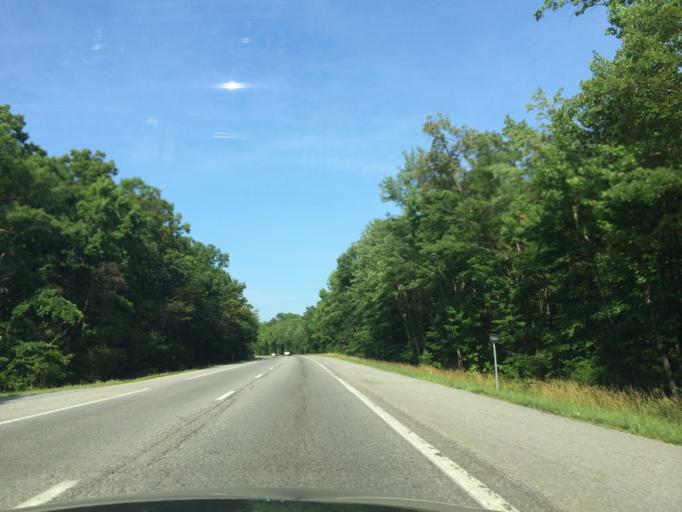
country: US
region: Maryland
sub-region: Prince George's County
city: Brandywine
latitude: 38.7054
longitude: -76.8594
